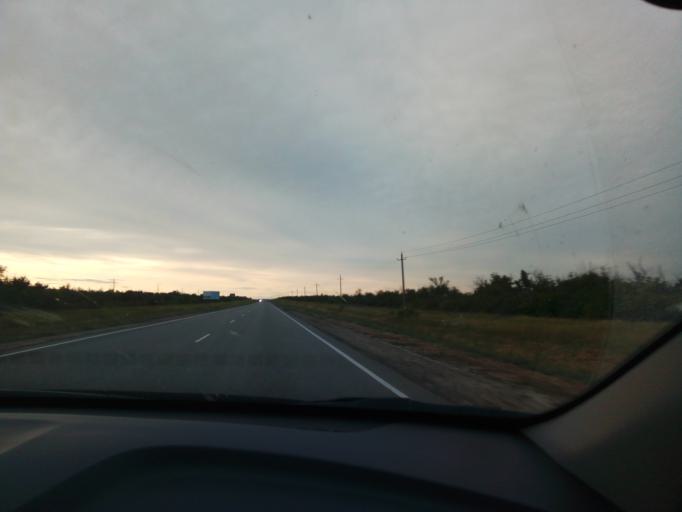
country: RU
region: Volgograd
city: Primorsk
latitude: 49.2729
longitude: 44.8756
